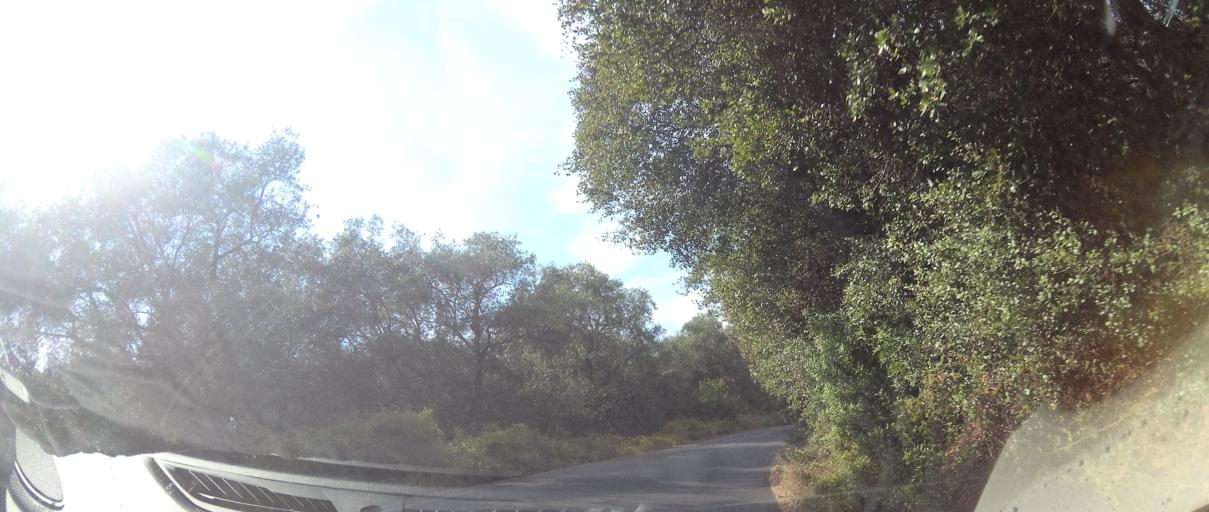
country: GR
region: Ionian Islands
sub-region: Nomos Kerkyras
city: Kynopiastes
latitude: 39.5474
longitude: 19.8676
